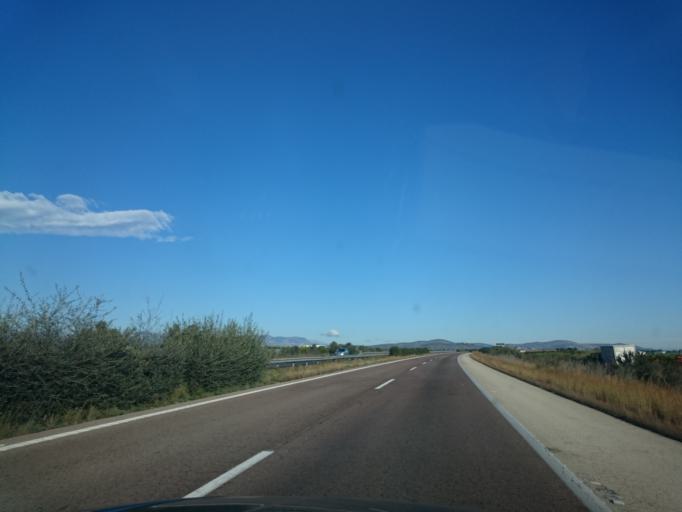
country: ES
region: Catalonia
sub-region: Provincia de Tarragona
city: Ulldecona
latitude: 40.5426
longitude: 0.4190
